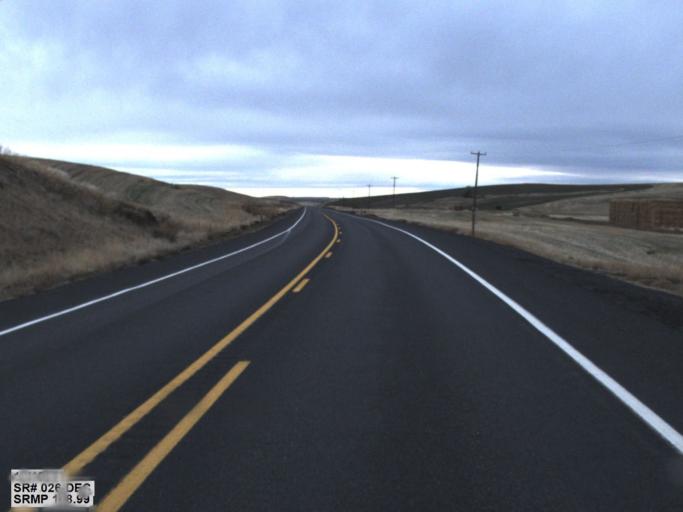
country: US
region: Washington
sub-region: Garfield County
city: Pomeroy
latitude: 46.8130
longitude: -117.8132
